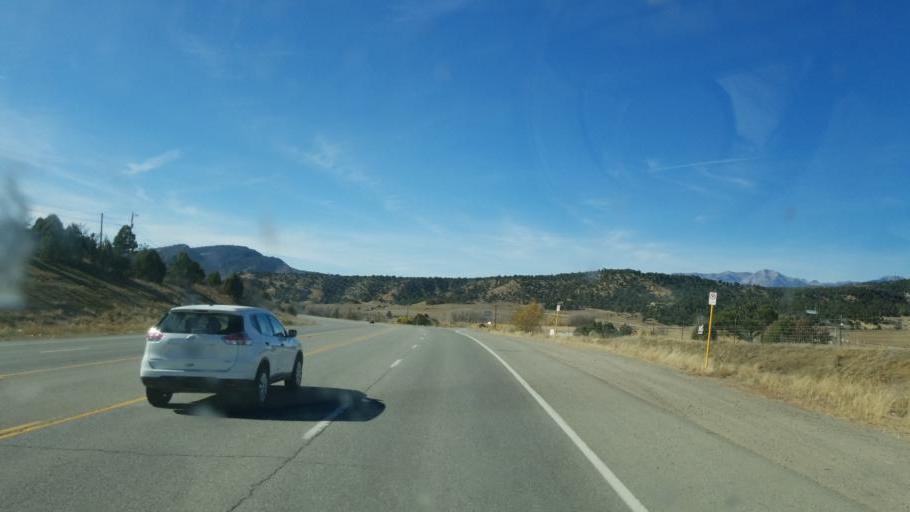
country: US
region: Colorado
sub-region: La Plata County
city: Durango
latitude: 37.2284
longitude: -107.8255
